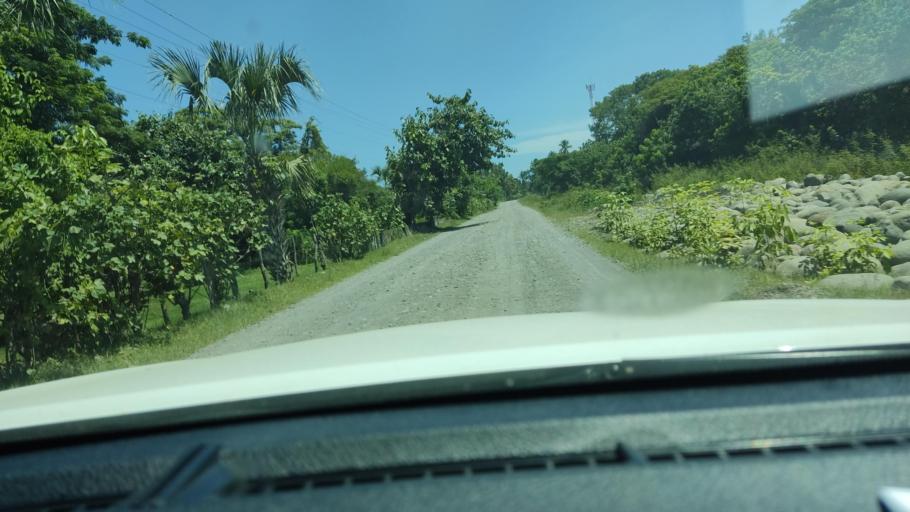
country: SV
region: Ahuachapan
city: San Francisco Menendez
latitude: 13.7555
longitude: -90.1199
